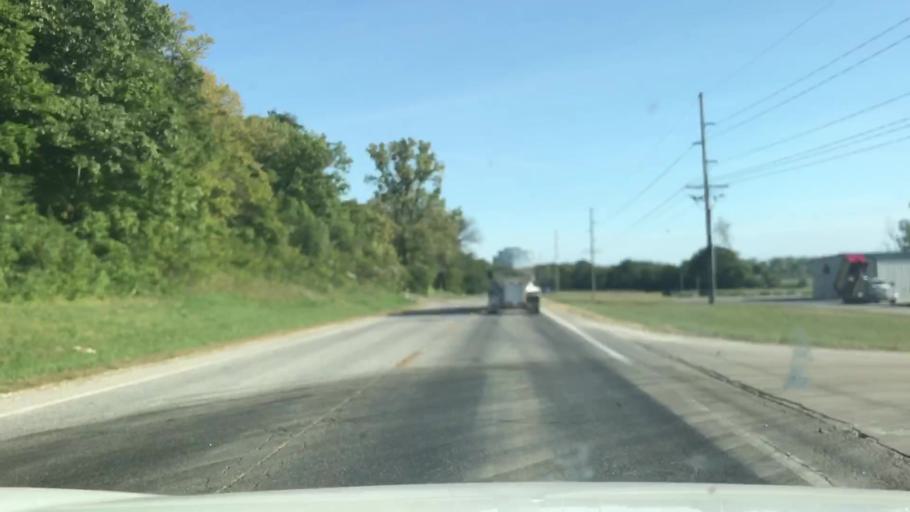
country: US
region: Illinois
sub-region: Adams County
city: Quincy
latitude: 39.8497
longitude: -91.3788
